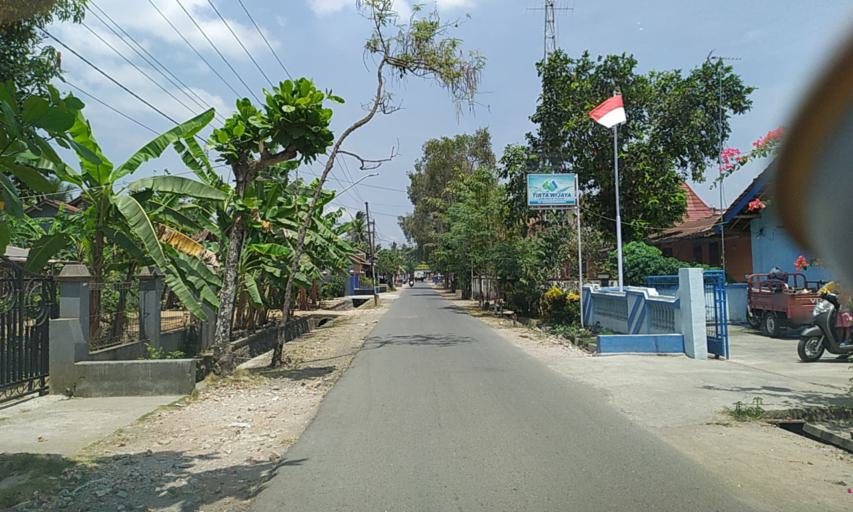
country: ID
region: Central Java
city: Gandrungmangu
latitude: -7.5222
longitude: 108.8561
